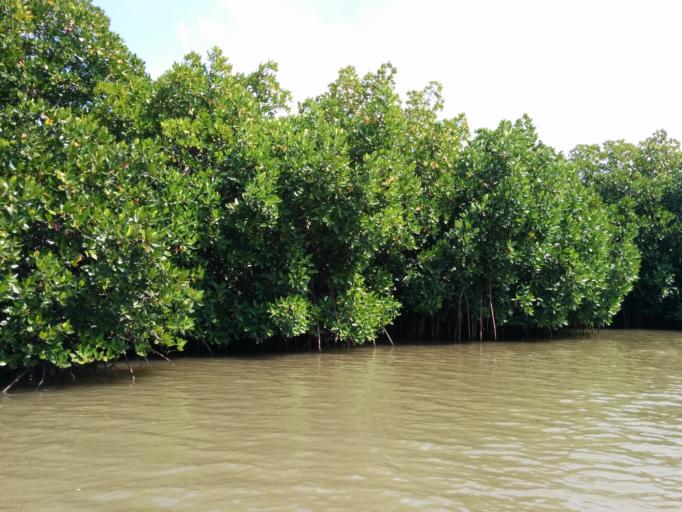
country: IN
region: Tamil Nadu
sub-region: Cuddalore
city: Annamalainagar
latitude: 11.4302
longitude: 79.7933
